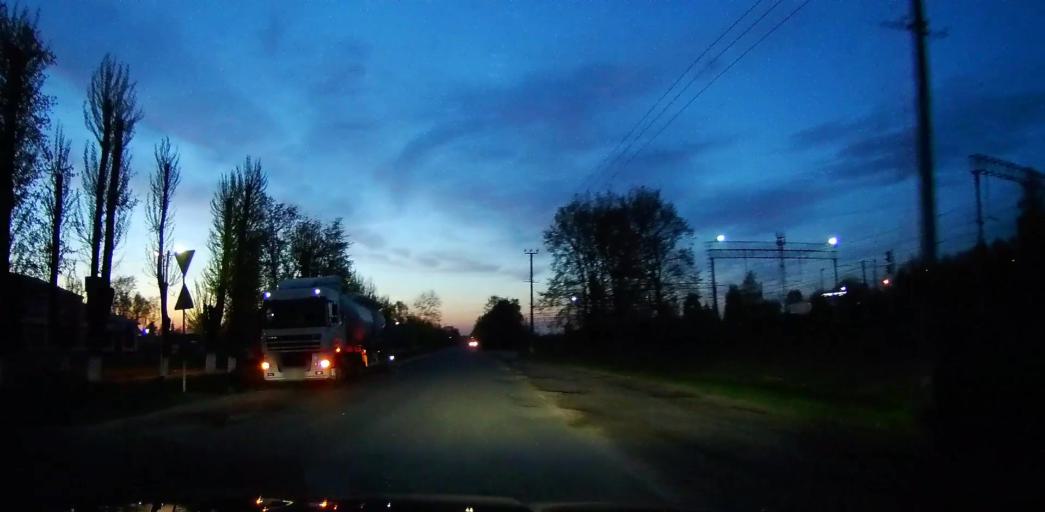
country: RU
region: Moskovskaya
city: Peski
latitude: 55.2097
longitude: 38.7728
